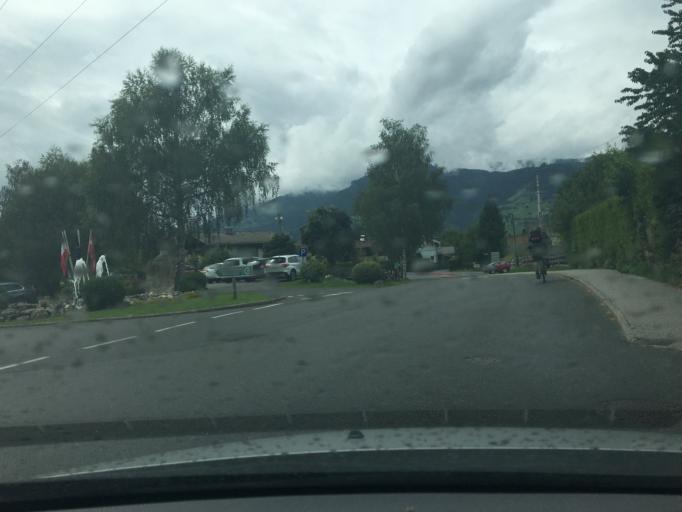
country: AT
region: Salzburg
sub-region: Politischer Bezirk Zell am See
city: Bruck an der Grossglocknerstrasse
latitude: 47.2841
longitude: 12.8179
